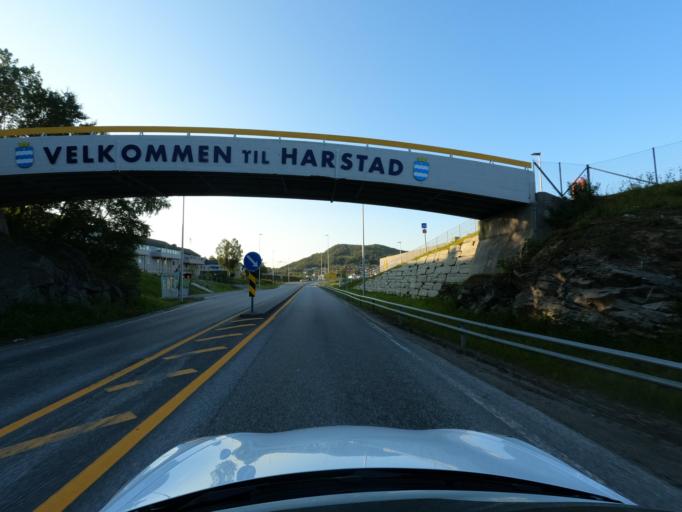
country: NO
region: Troms
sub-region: Harstad
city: Harstad
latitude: 68.7786
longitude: 16.5638
